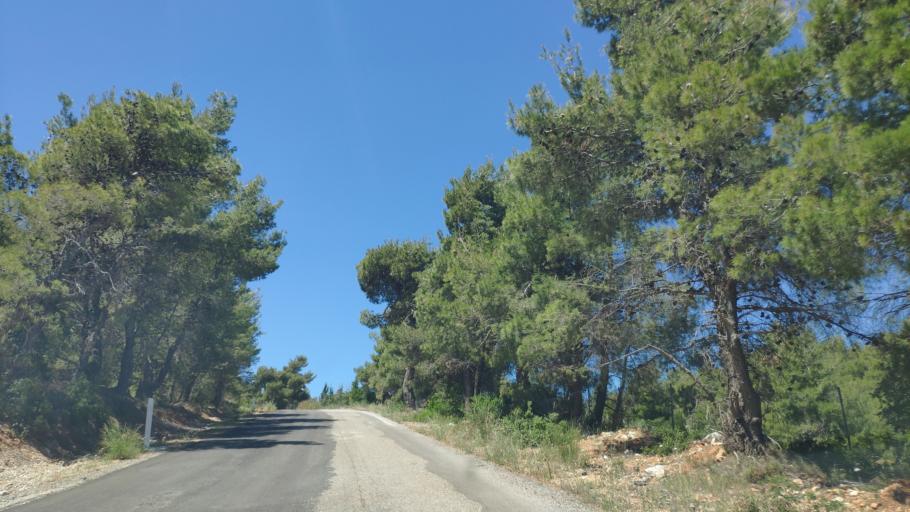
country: GR
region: Central Greece
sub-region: Nomos Voiotias
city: Kaparellion
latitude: 38.2052
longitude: 23.1653
